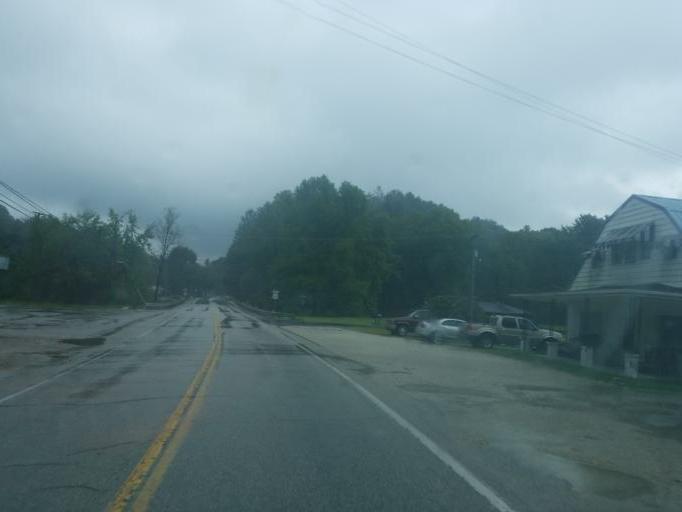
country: US
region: Kentucky
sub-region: Rowan County
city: Morehead
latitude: 38.2426
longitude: -83.3458
